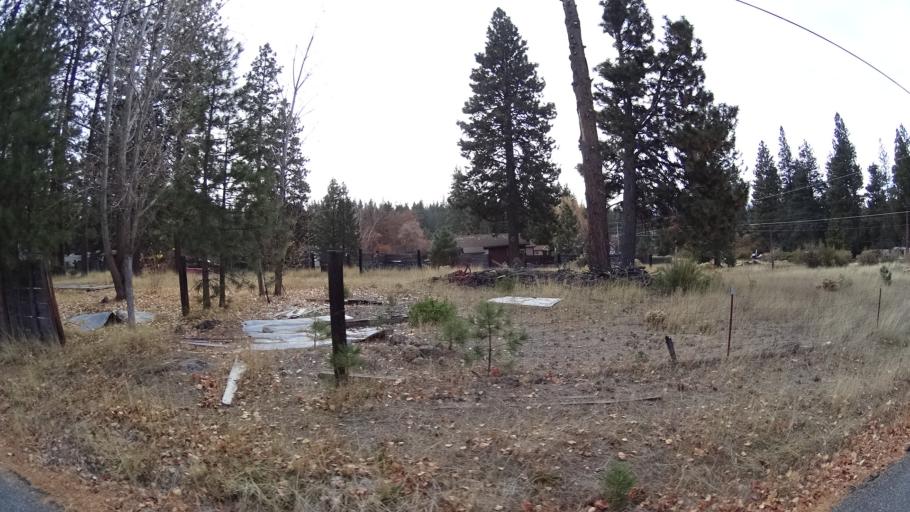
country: US
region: California
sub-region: Siskiyou County
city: Weed
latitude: 41.4477
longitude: -122.3613
